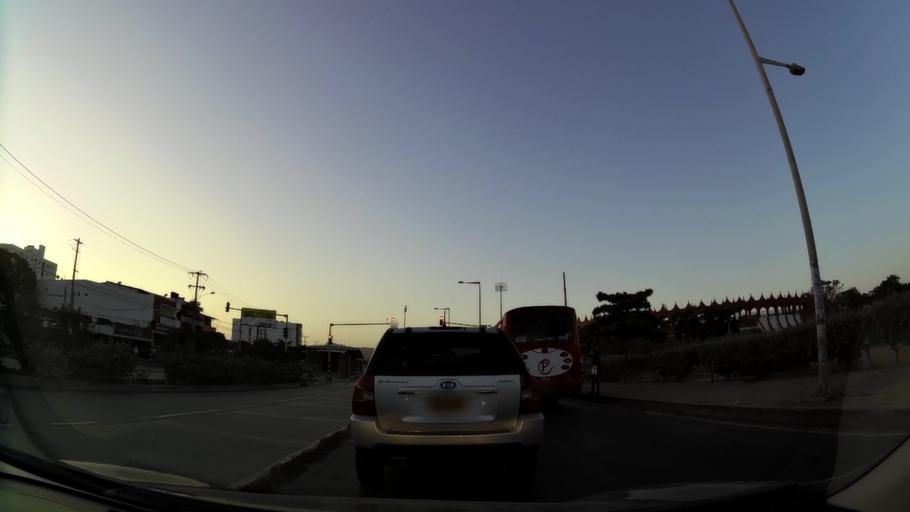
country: CO
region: Bolivar
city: Cartagena
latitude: 10.4033
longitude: -75.4966
